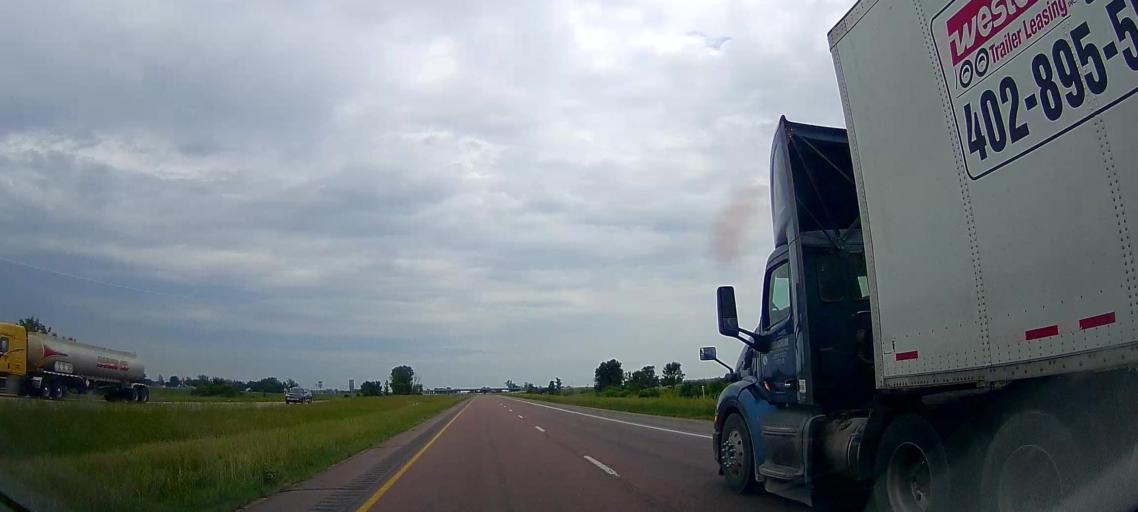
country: US
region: Iowa
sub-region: Woodbury County
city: Sergeant Bluff
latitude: 42.3157
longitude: -96.3063
